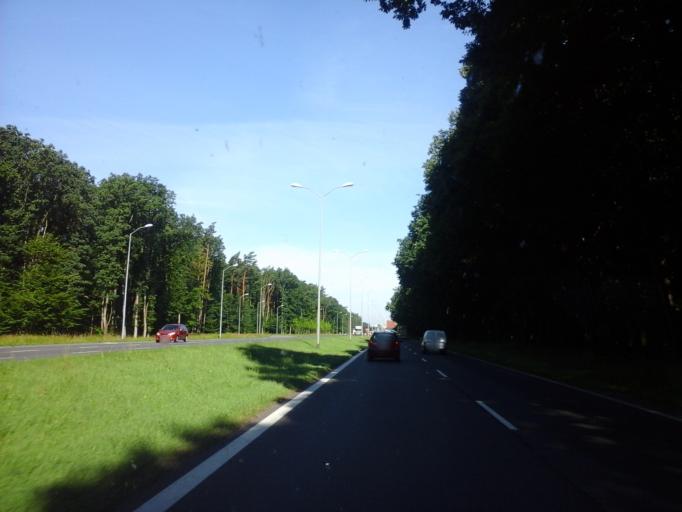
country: PL
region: West Pomeranian Voivodeship
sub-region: Powiat gryfinski
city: Stare Czarnowo
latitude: 53.3692
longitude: 14.7182
